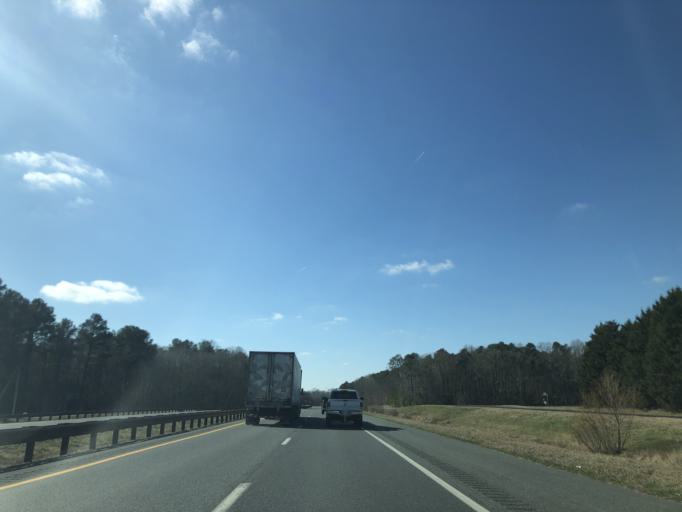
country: US
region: Maryland
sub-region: Worcester County
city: Berlin
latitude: 38.2750
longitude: -75.2386
